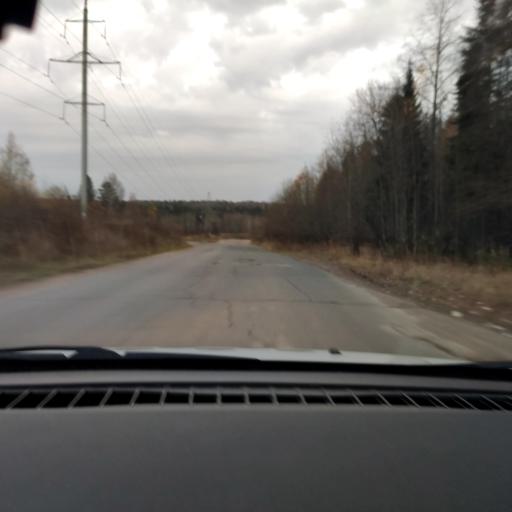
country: RU
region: Perm
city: Perm
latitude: 58.0892
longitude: 56.4170
